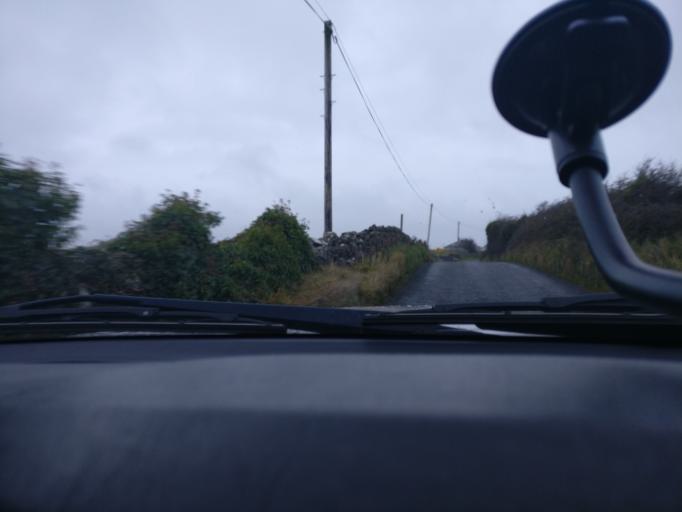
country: IE
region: Connaught
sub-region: County Galway
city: Loughrea
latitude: 53.2116
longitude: -8.5482
